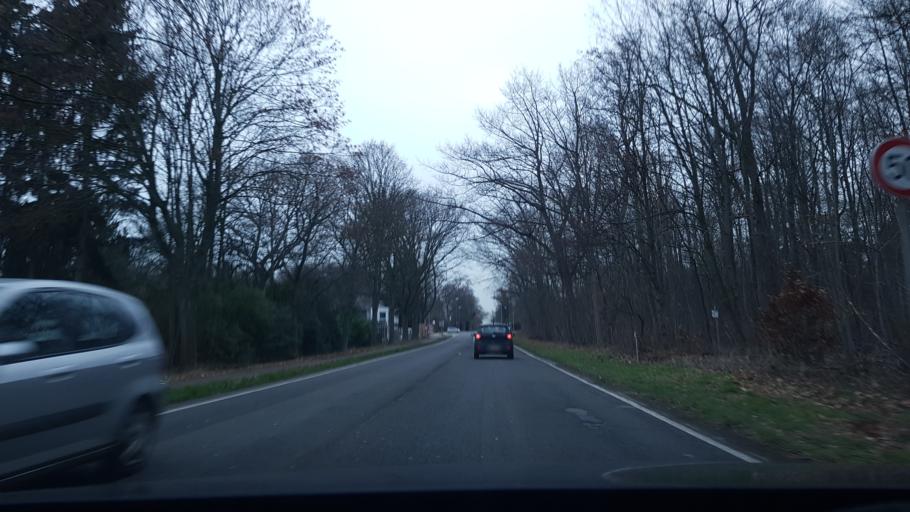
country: DE
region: North Rhine-Westphalia
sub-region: Regierungsbezirk Dusseldorf
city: Moers
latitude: 51.4294
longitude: 6.6494
